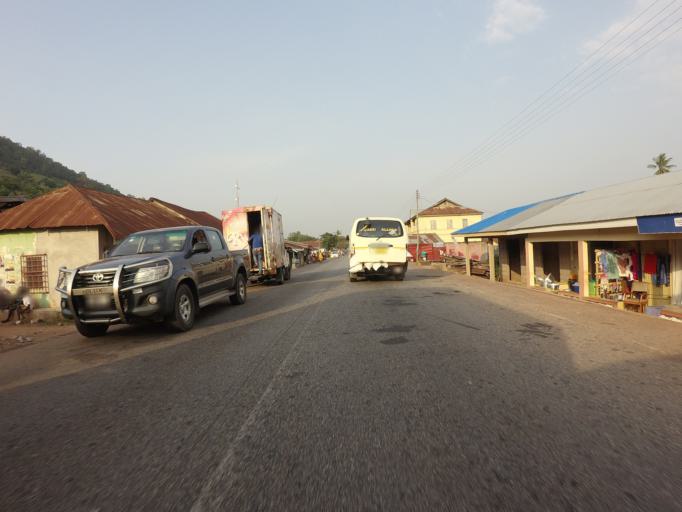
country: GH
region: Volta
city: Ho
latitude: 6.5409
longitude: 0.2874
